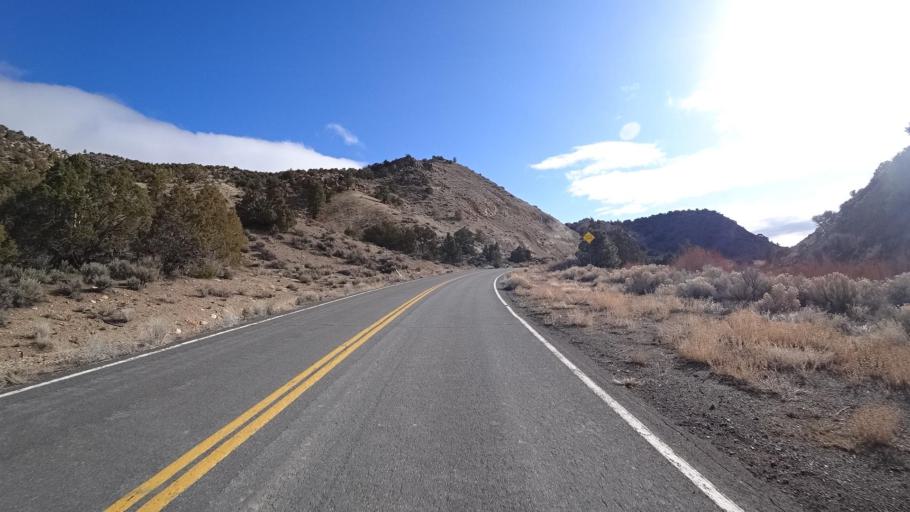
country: US
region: Nevada
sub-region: Washoe County
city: Cold Springs
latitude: 39.9043
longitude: -119.9936
